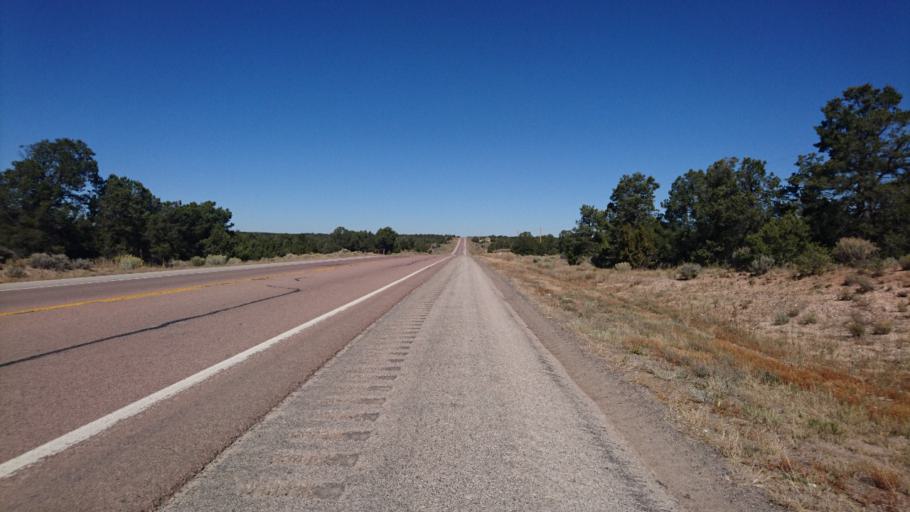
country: US
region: New Mexico
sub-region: McKinley County
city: Gallup
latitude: 35.3129
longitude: -108.7576
